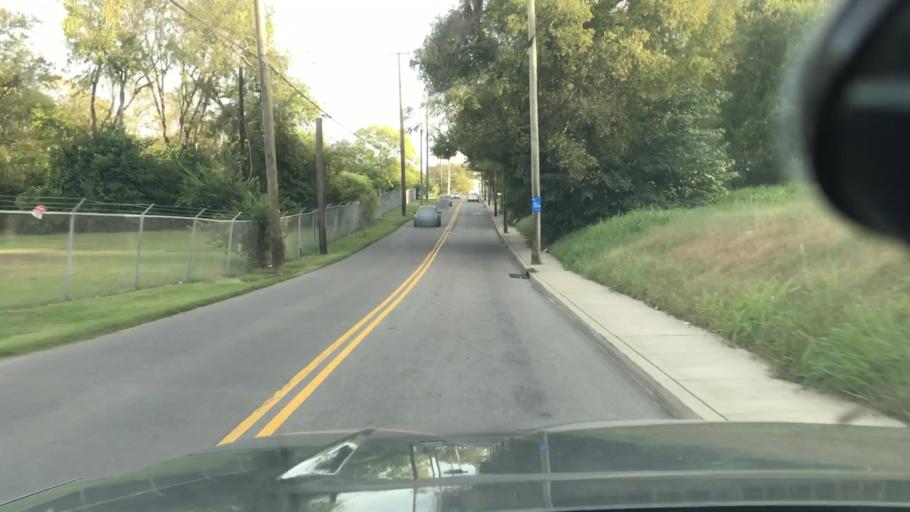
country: US
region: Tennessee
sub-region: Davidson County
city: Nashville
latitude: 36.1871
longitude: -86.7936
